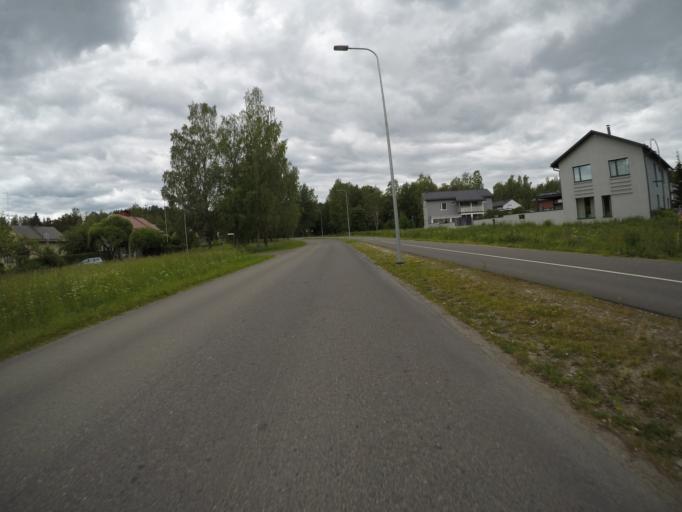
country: FI
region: Haeme
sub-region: Haemeenlinna
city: Haemeenlinna
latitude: 60.9903
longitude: 24.4320
